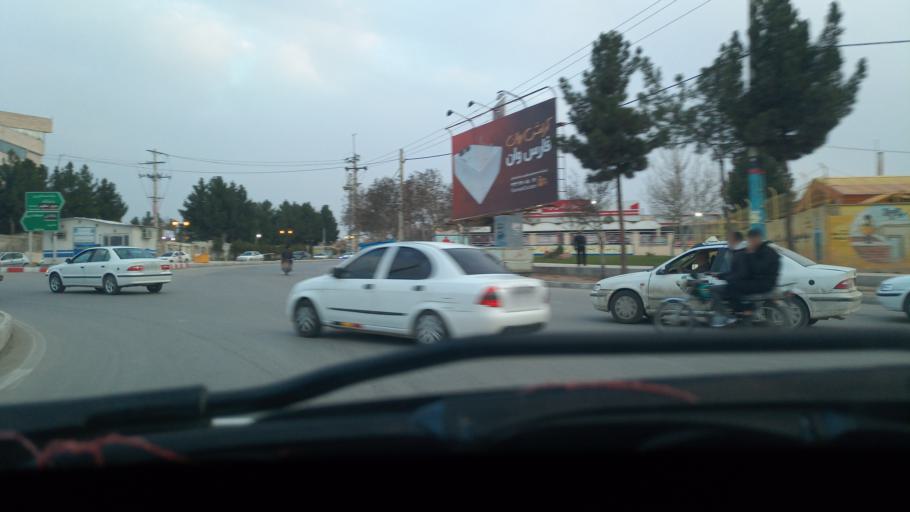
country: IR
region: Khorasan-e Shomali
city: Bojnurd
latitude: 37.4622
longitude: 57.3325
